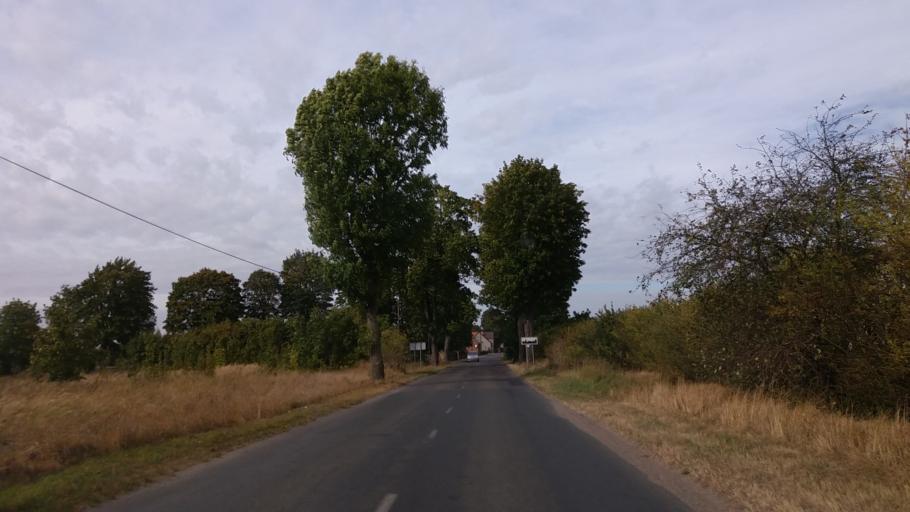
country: PL
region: Lubusz
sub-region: Powiat strzelecko-drezdenecki
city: Strzelce Krajenskie
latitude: 52.9483
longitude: 15.4546
